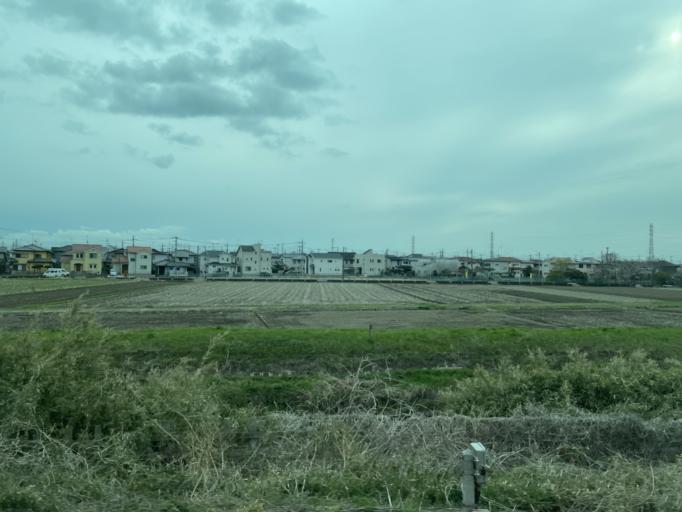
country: JP
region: Saitama
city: Kukichuo
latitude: 36.0448
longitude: 139.6942
